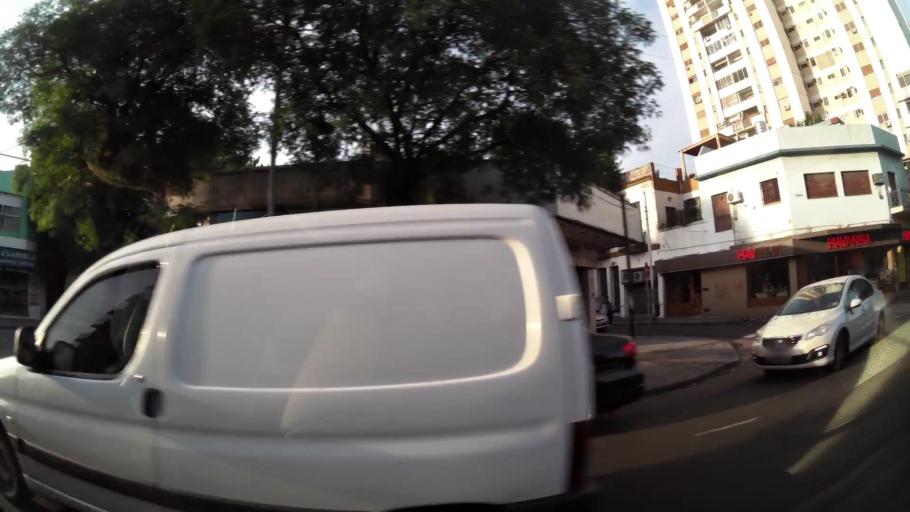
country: AR
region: Buenos Aires F.D.
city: Villa Santa Rita
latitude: -34.6349
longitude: -58.4368
